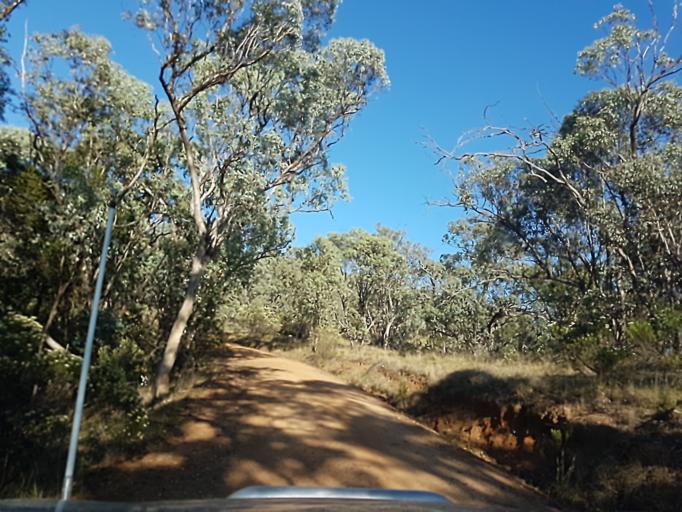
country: AU
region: New South Wales
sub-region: Snowy River
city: Jindabyne
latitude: -36.9555
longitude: 148.3635
